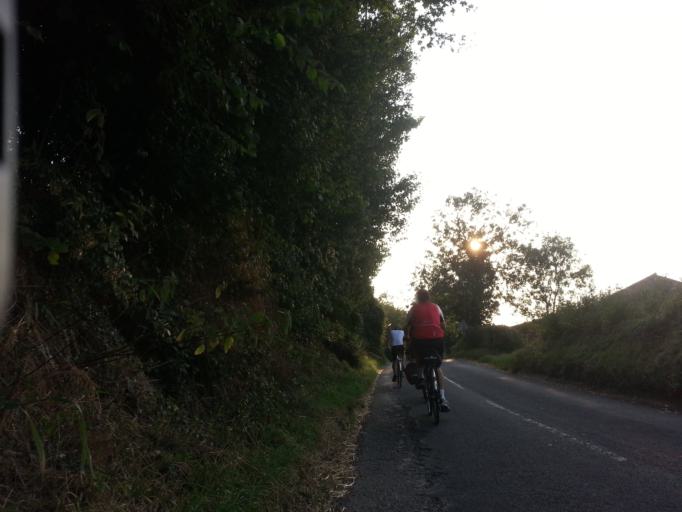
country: GB
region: England
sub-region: Suffolk
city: Wattisham
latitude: 52.1059
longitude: 1.0009
